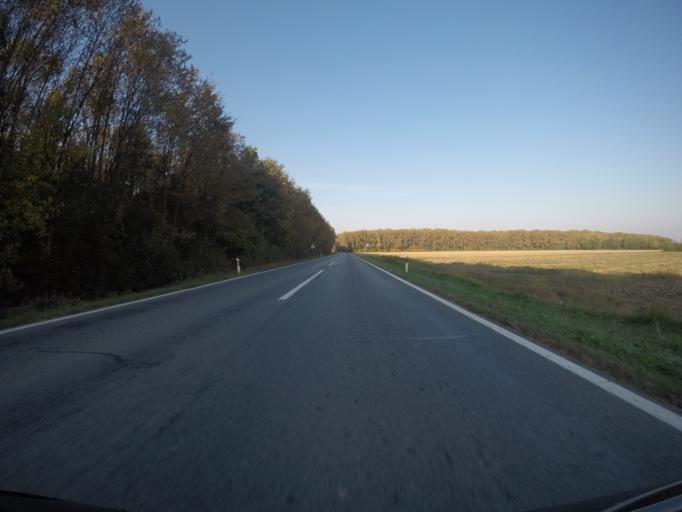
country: HR
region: Virovitick-Podravska
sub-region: Grad Virovitica
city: Virovitica
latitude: 45.8788
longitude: 17.4058
